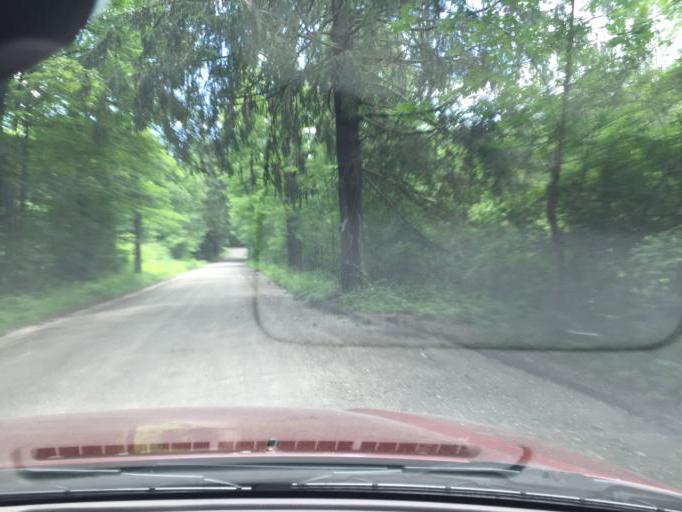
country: US
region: Connecticut
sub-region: Litchfield County
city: Litchfield
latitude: 41.7549
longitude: -73.2234
